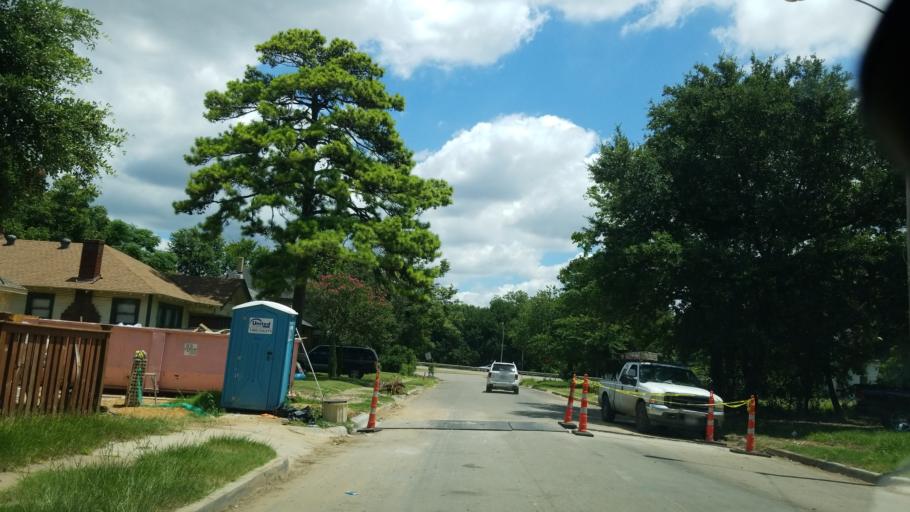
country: US
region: Texas
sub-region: Dallas County
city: Dallas
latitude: 32.7513
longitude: -96.7643
